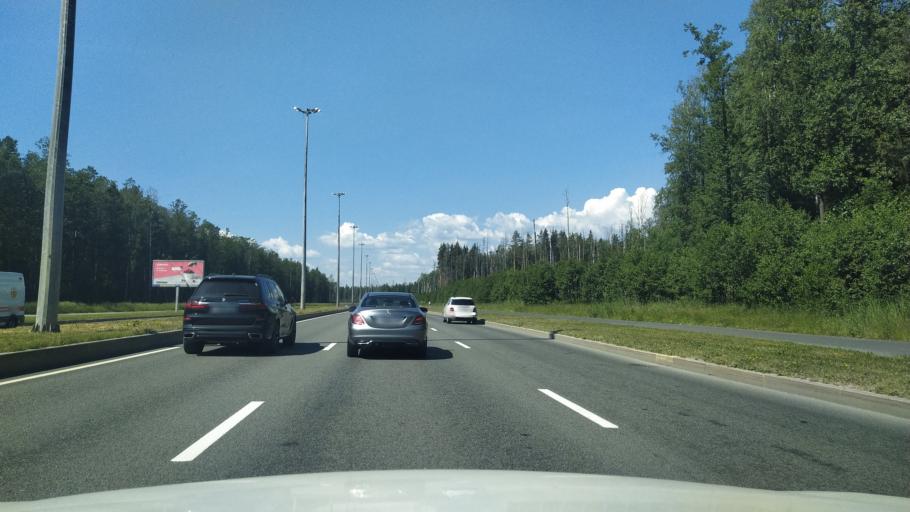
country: RU
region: Leningrad
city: Untolovo
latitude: 60.0572
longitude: 30.2220
